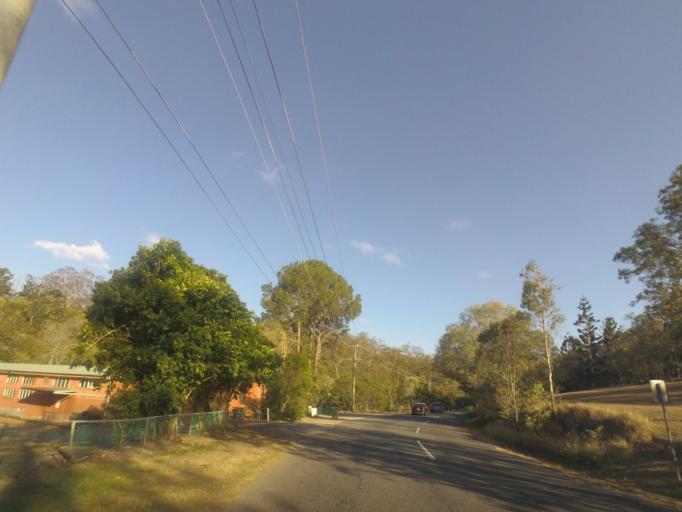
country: AU
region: Queensland
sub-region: Brisbane
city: Taringa
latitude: -27.4664
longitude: 152.9690
